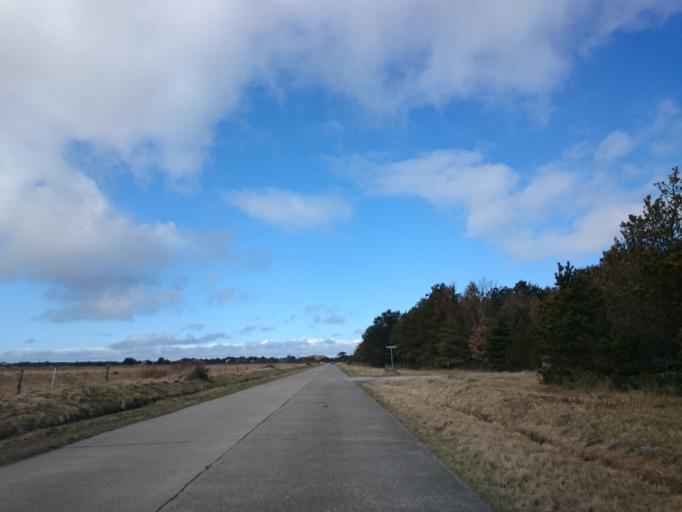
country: DK
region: North Denmark
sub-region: Frederikshavn Kommune
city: Skagen
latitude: 57.6592
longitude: 10.4051
